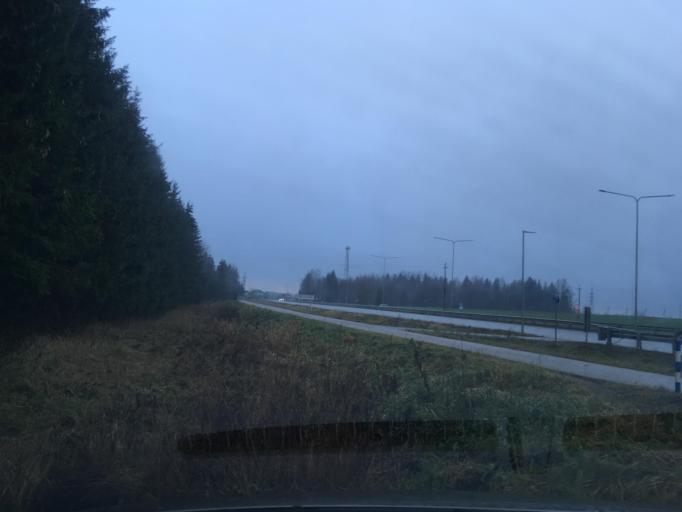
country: EE
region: Tartu
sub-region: Tartu linn
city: Tartu
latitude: 58.3729
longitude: 26.7909
